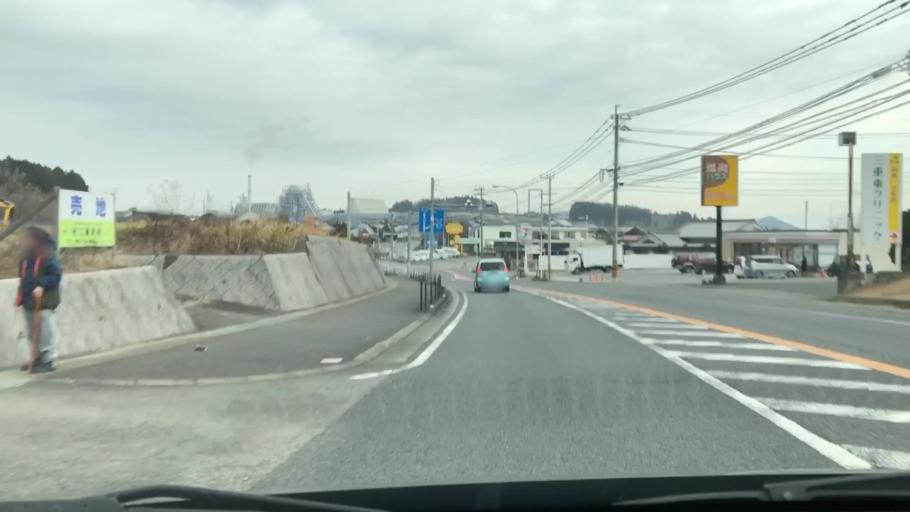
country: JP
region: Oita
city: Takedamachi
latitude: 32.9951
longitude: 131.6156
